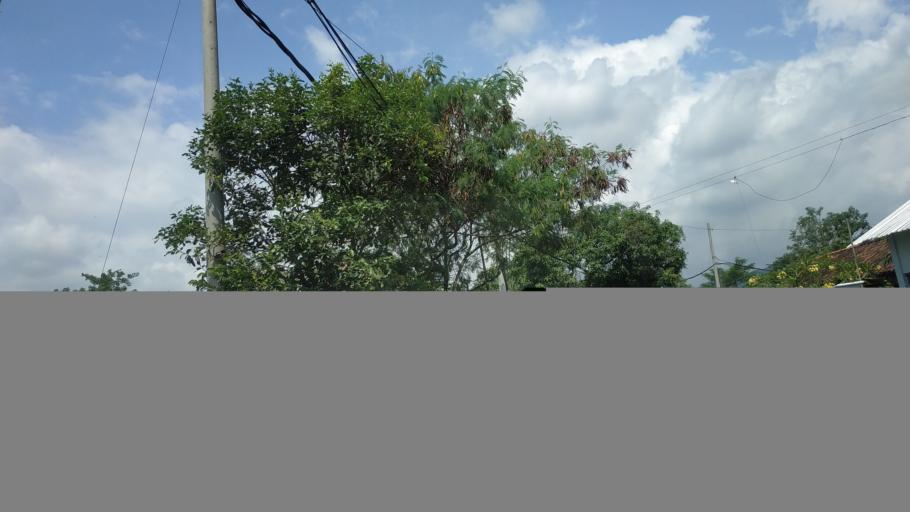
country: ID
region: Central Java
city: Weleri
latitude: -6.9938
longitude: 110.0745
